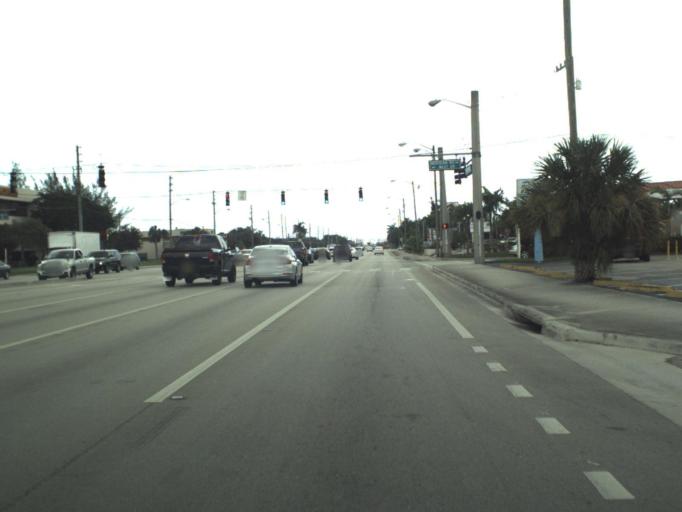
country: US
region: Florida
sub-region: Palm Beach County
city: Plantation Mobile Home Park
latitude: 26.7073
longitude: -80.1344
